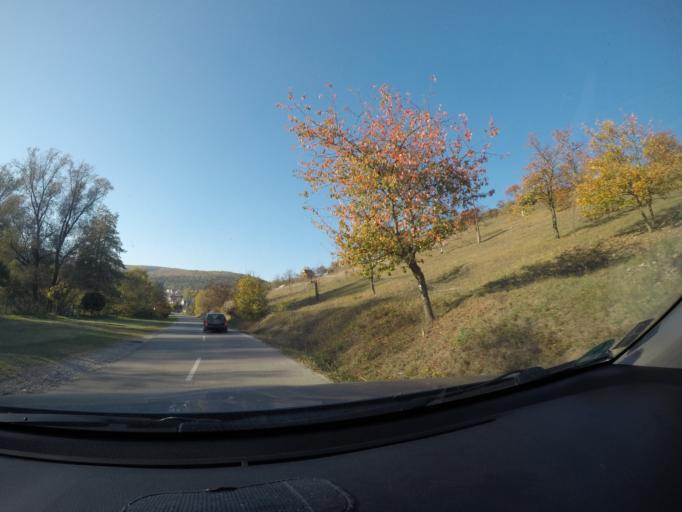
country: SK
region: Nitriansky
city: Nemsova
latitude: 48.9757
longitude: 18.0770
